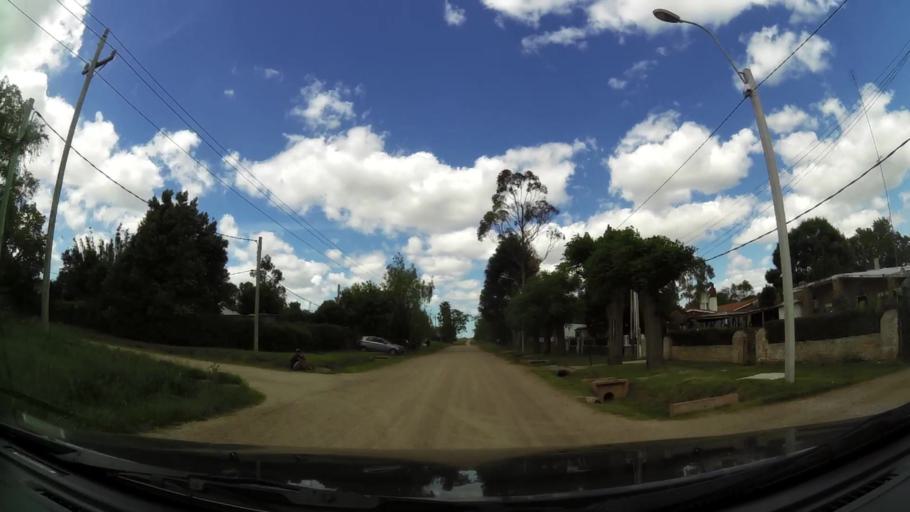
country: UY
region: Canelones
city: Colonia Nicolich
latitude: -34.8134
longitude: -56.0449
